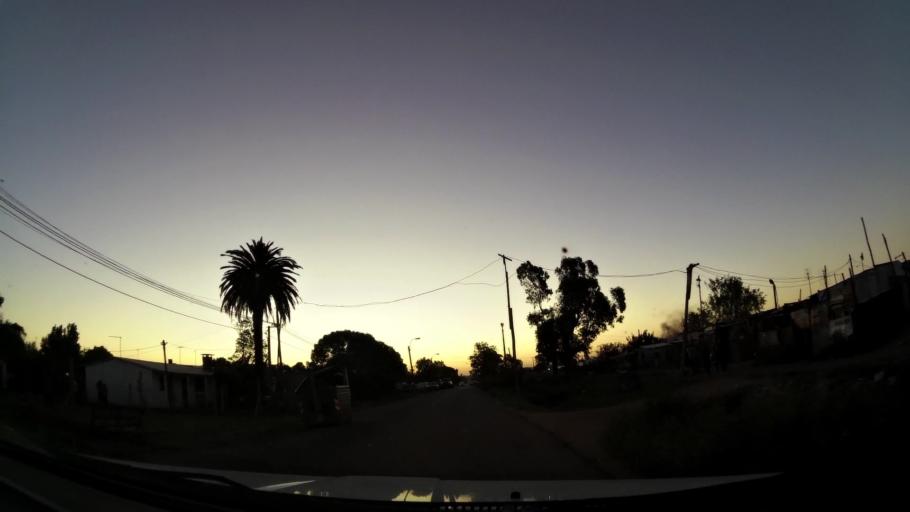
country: UY
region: Montevideo
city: Montevideo
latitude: -34.8228
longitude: -56.1633
